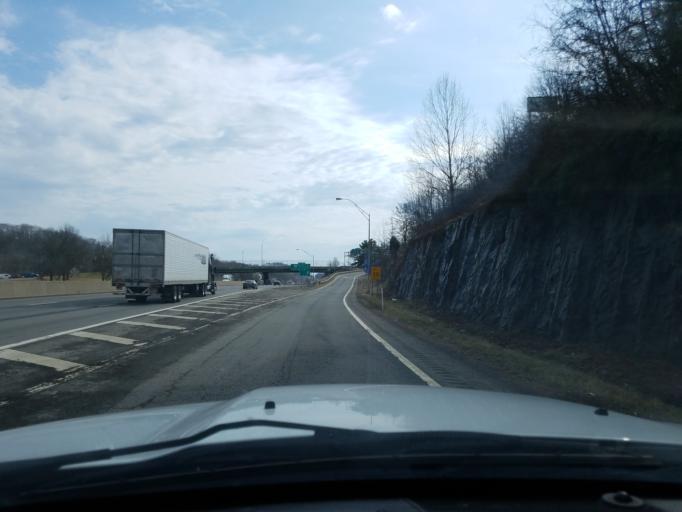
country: US
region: West Virginia
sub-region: Kanawha County
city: Cross Lanes
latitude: 38.4150
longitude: -81.7979
